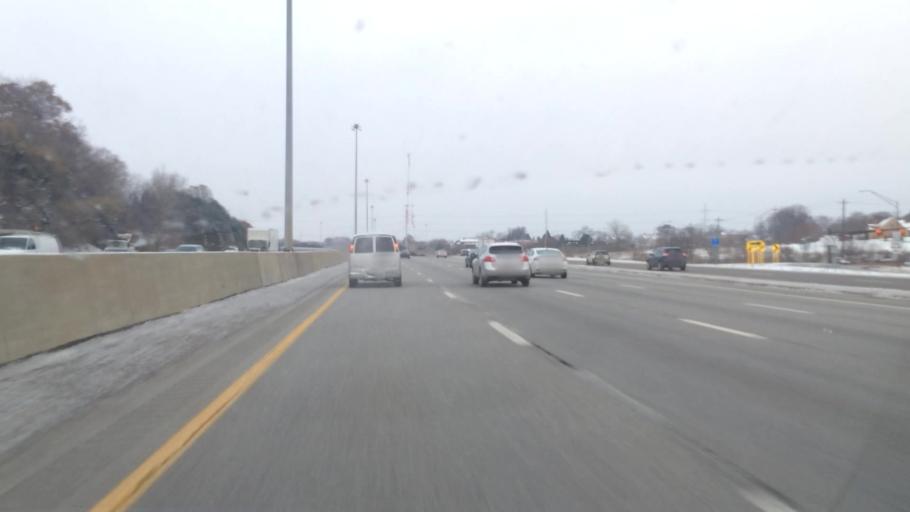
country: US
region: Ohio
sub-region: Cuyahoga County
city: Brooklyn Heights
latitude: 41.4153
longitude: -81.6751
